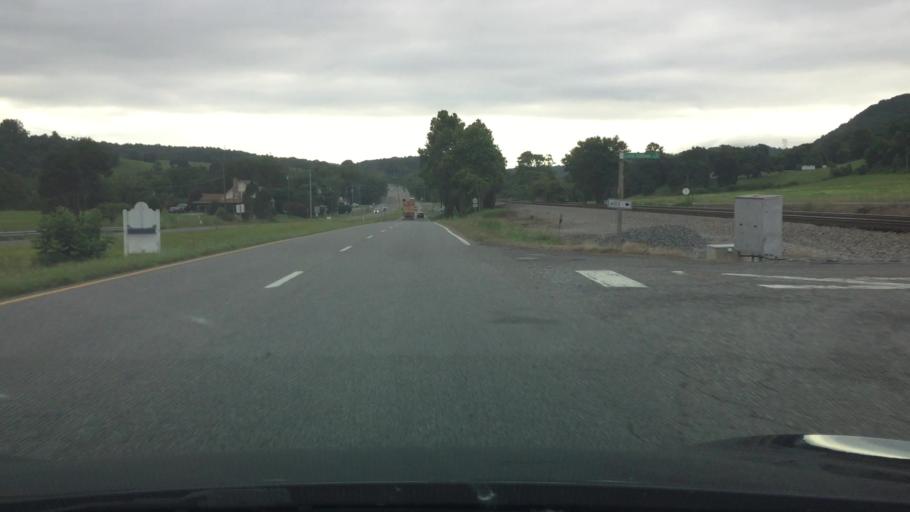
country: US
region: Virginia
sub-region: Montgomery County
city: Shawsville
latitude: 37.2310
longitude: -80.1999
